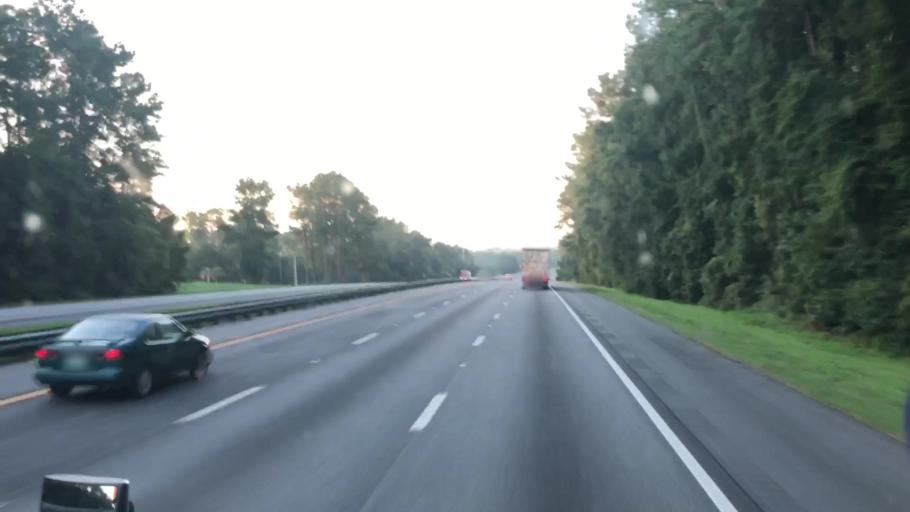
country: US
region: Florida
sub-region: Alachua County
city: High Springs
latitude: 29.8188
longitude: -82.5169
